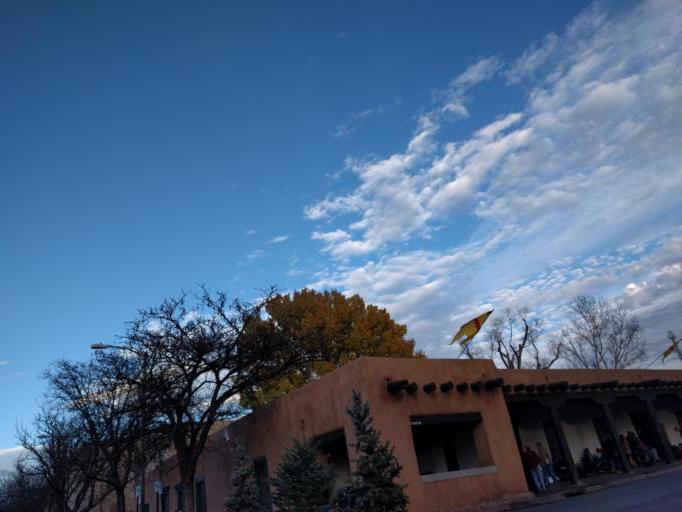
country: US
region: New Mexico
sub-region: Santa Fe County
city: Santa Fe
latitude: 35.6878
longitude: -105.9388
